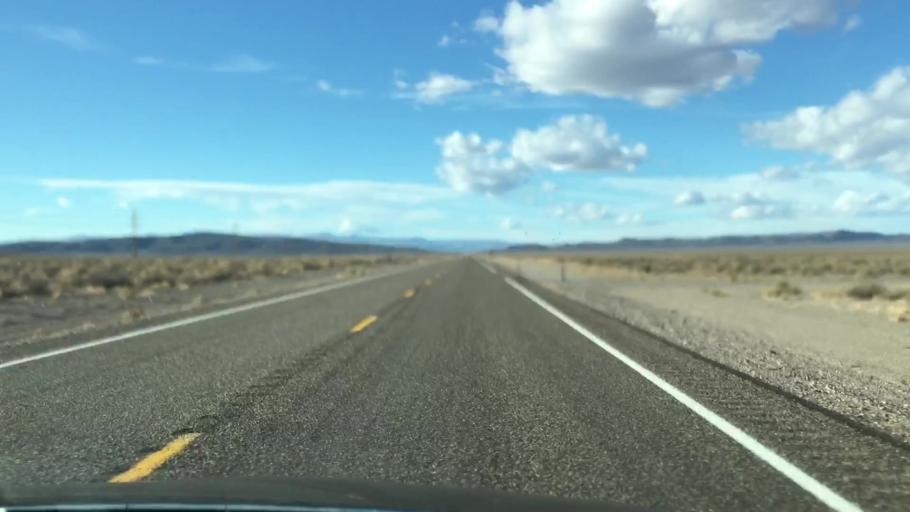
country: US
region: Nevada
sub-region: Nye County
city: Beatty
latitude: 37.1310
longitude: -116.8421
